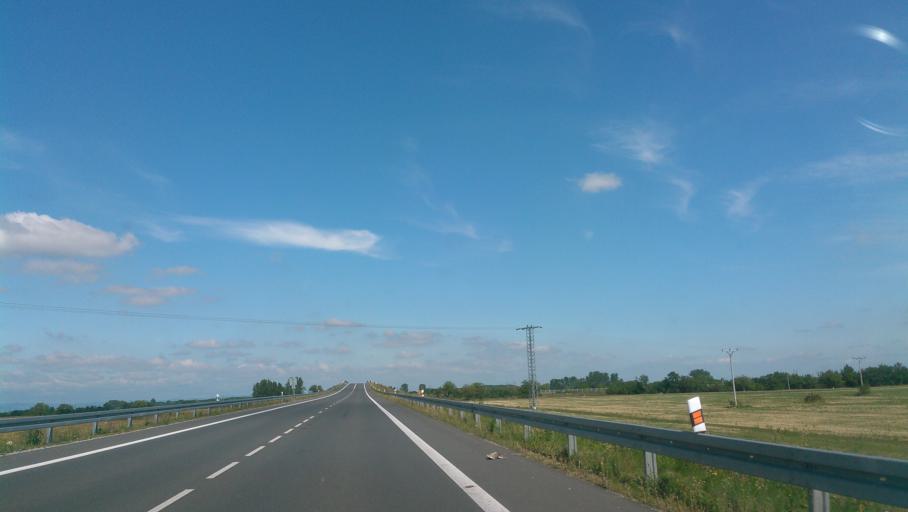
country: SK
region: Trnavsky
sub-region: Okres Galanta
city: Galanta
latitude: 48.1824
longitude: 17.7029
